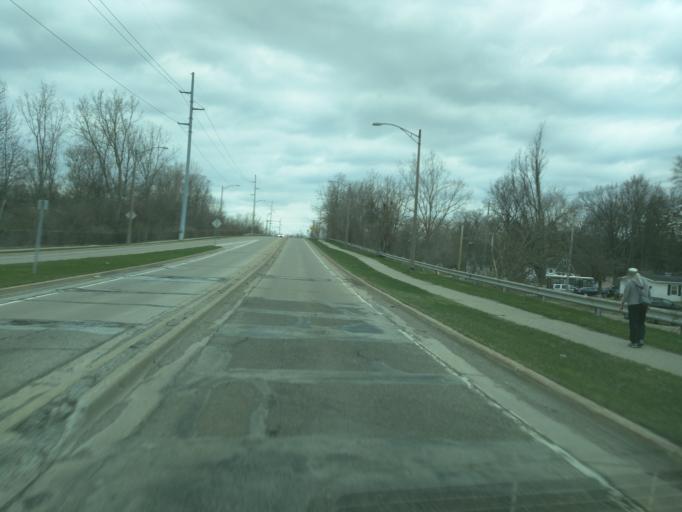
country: US
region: Michigan
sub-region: Ingham County
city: Lansing
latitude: 42.7212
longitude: -84.5223
